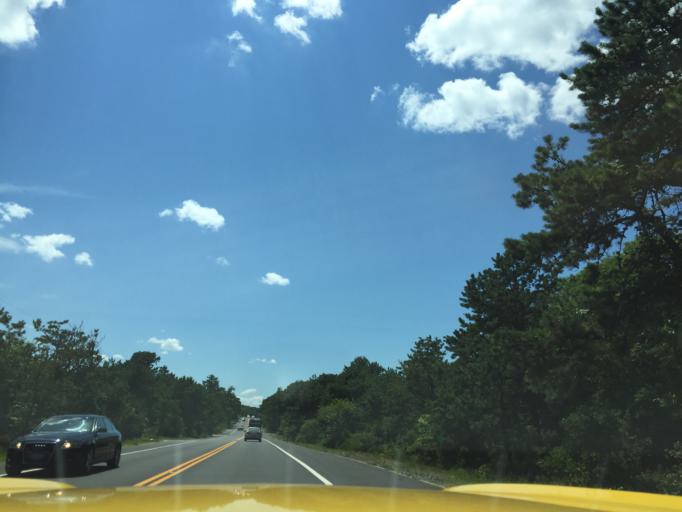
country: US
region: New York
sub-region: Suffolk County
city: Amagansett
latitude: 40.9807
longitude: -72.1071
